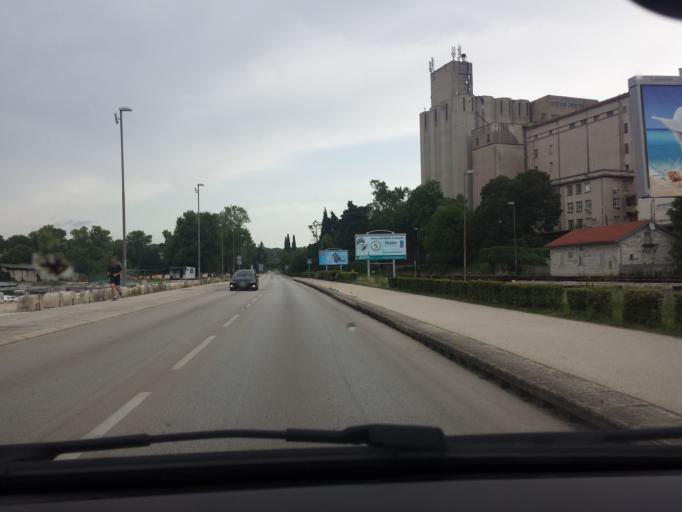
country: HR
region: Istarska
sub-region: Grad Pula
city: Pula
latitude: 44.8823
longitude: 13.8479
